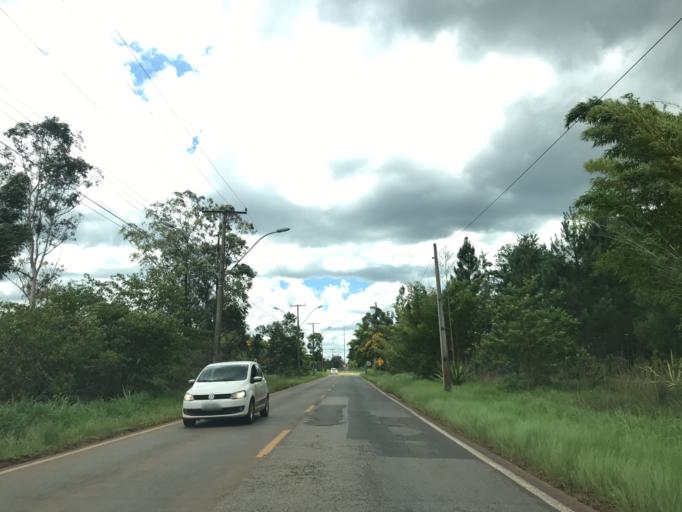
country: BR
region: Federal District
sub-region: Brasilia
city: Brasilia
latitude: -15.8964
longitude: -47.9399
